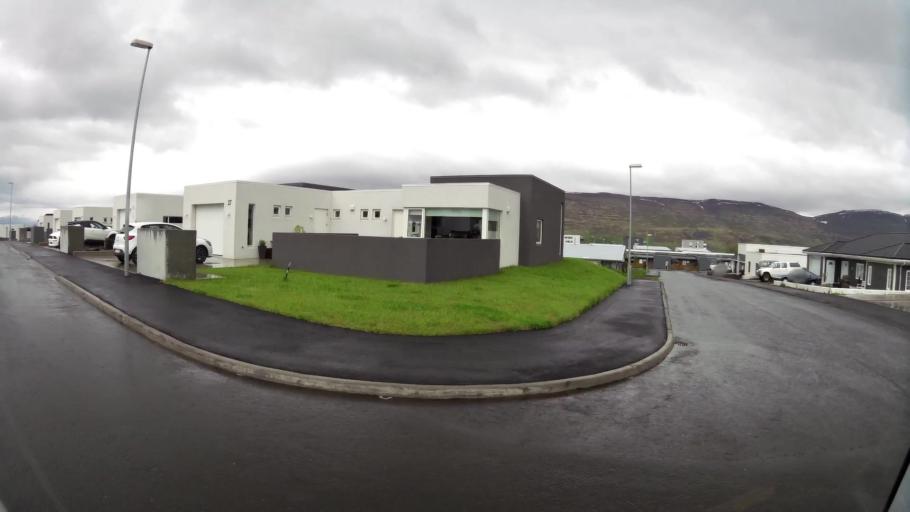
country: IS
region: Northeast
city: Akureyri
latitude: 65.6618
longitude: -18.1057
